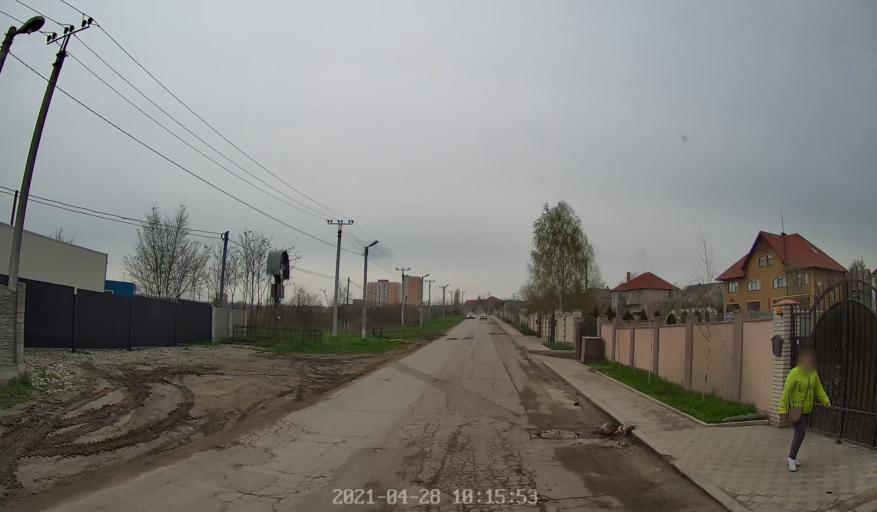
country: MD
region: Chisinau
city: Chisinau
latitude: 46.9888
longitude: 28.9333
